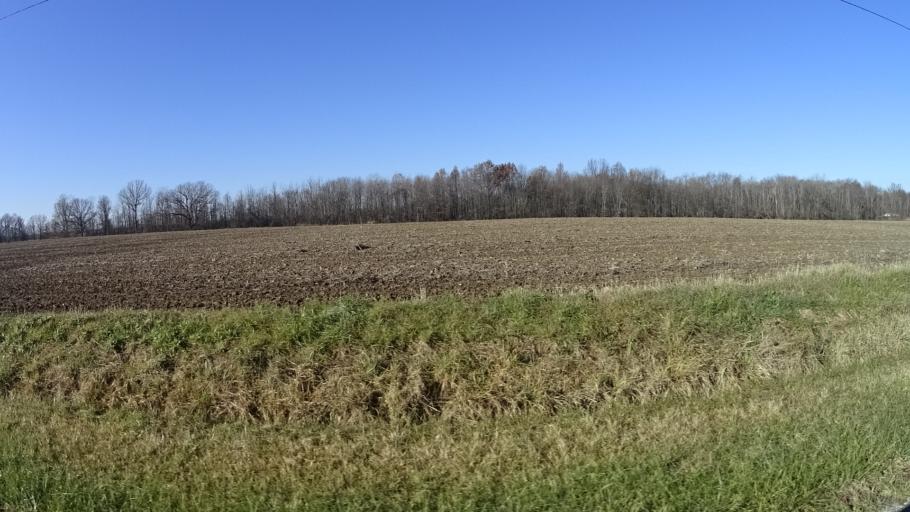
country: US
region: Ohio
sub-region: Lorain County
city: Wellington
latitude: 41.0915
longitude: -82.1810
